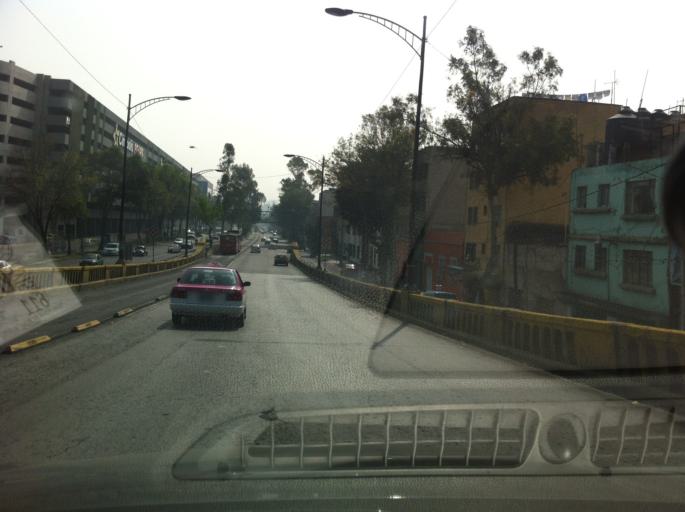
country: MX
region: Mexico City
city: Cuauhtemoc
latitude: 19.4530
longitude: -99.1521
